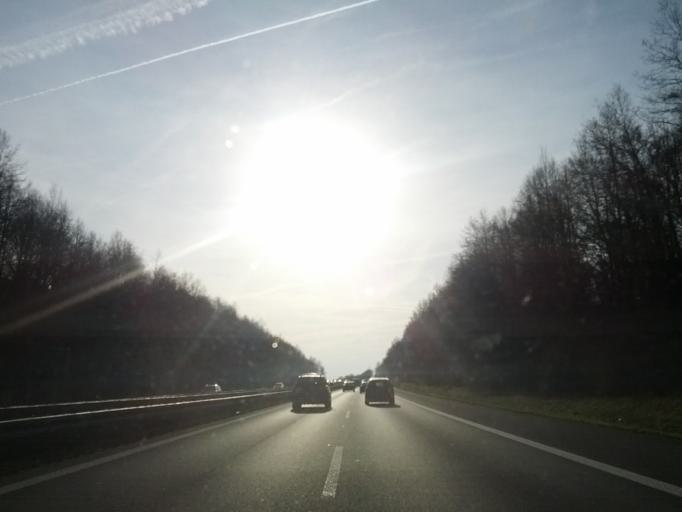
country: DE
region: Bavaria
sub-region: Regierungsbezirk Unterfranken
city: Rottendorf
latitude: 49.8202
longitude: 10.0435
